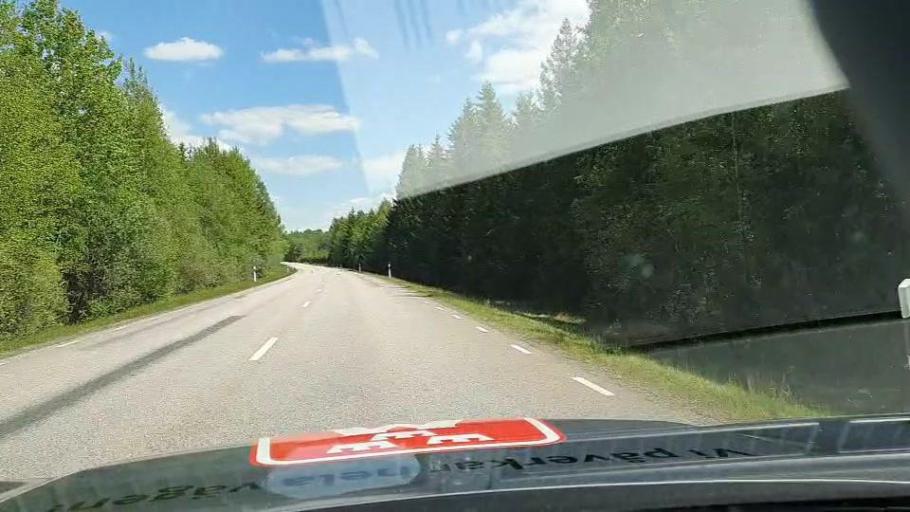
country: SE
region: Kronoberg
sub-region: Alvesta Kommun
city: Moheda
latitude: 57.0607
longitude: 14.5998
